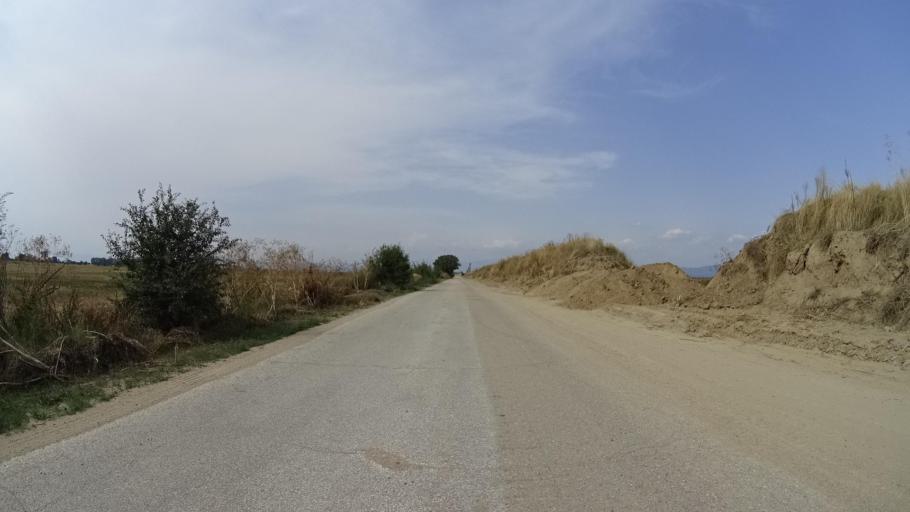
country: BG
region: Plovdiv
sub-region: Obshtina Kaloyanovo
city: Kaloyanovo
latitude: 42.3082
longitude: 24.7996
